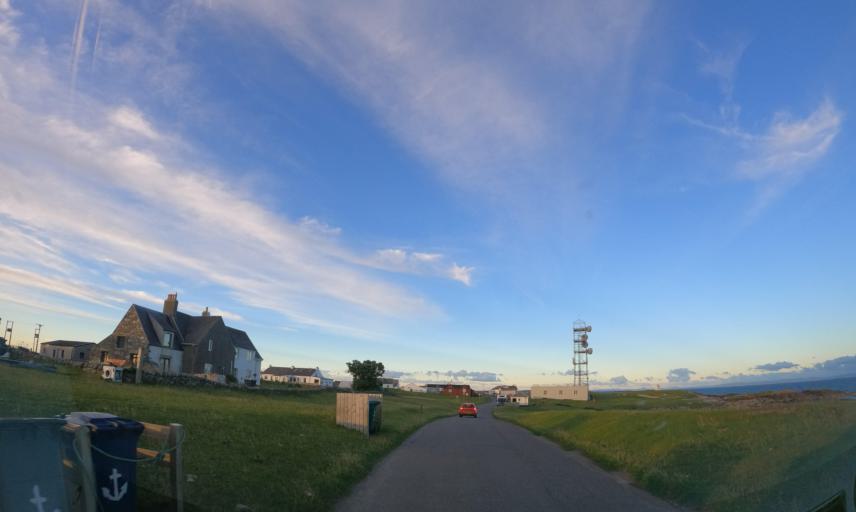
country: GB
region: Scotland
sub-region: Eilean Siar
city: Barra
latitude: 56.4992
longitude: -6.8090
